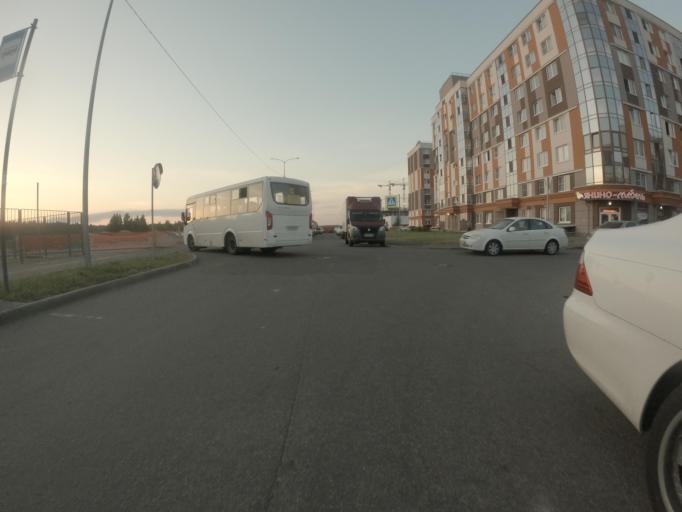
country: RU
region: Leningrad
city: Yanino Vtoroye
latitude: 59.9591
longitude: 30.6007
